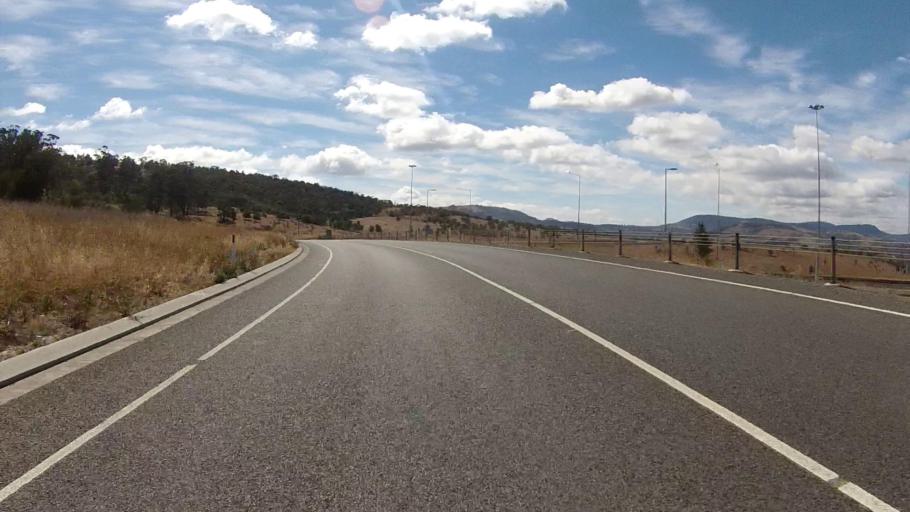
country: AU
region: Tasmania
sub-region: Brighton
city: Bridgewater
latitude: -42.7119
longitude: 147.2313
